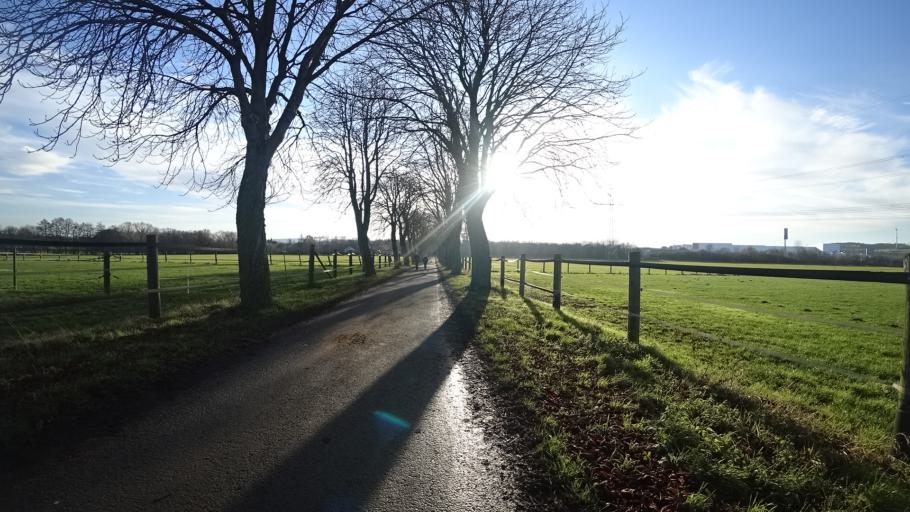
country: DE
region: Lower Saxony
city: Lauenau
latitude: 52.2809
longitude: 9.3561
